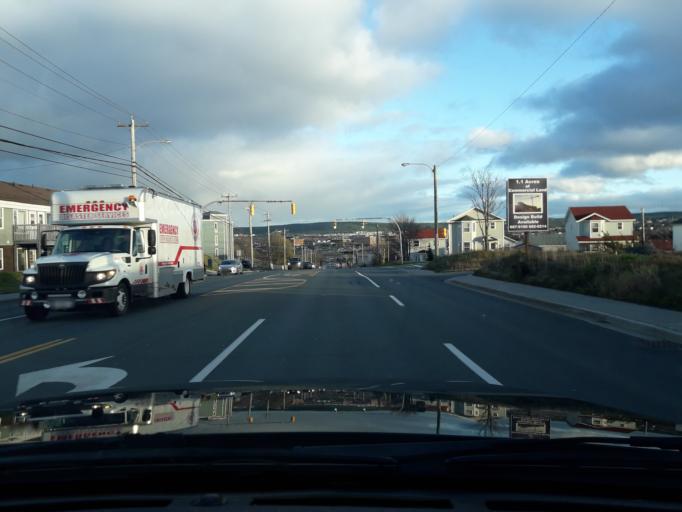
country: CA
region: Newfoundland and Labrador
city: St. John's
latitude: 47.5638
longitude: -52.7606
